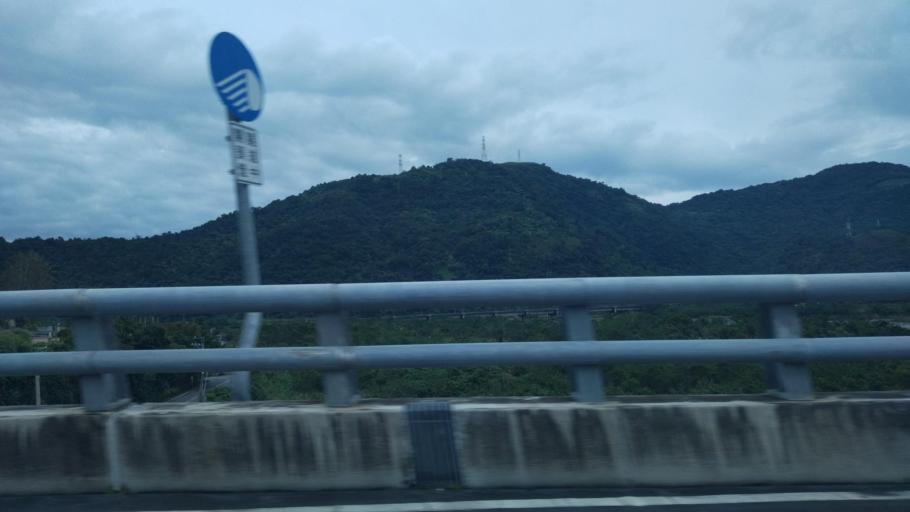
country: TW
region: Taiwan
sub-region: Yilan
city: Yilan
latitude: 24.4423
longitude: 121.7741
